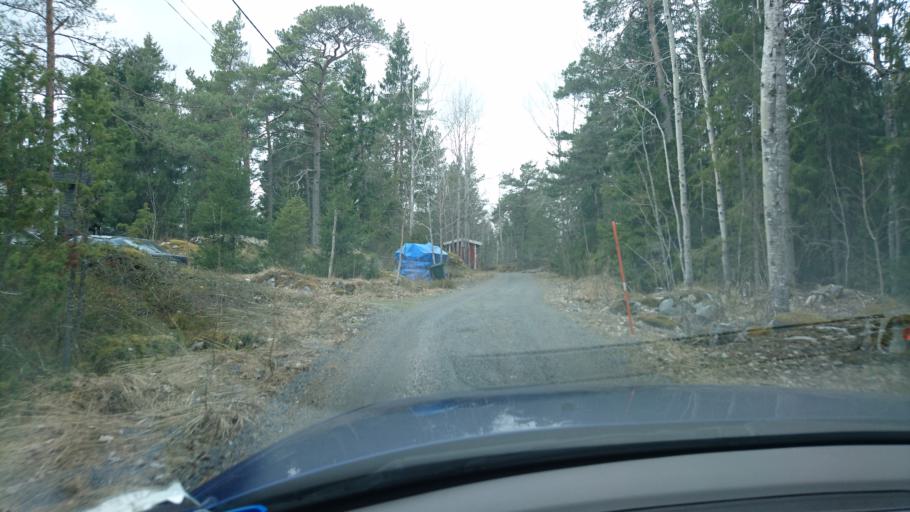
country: SE
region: Stockholm
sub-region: Norrtalje Kommun
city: Bjorko
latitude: 59.7887
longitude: 18.9889
